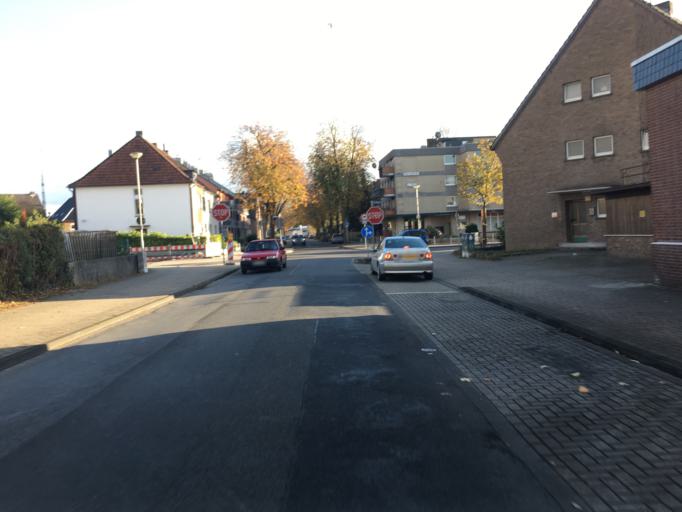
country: DE
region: North Rhine-Westphalia
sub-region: Regierungsbezirk Dusseldorf
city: Emmerich
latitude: 51.8395
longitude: 6.2432
